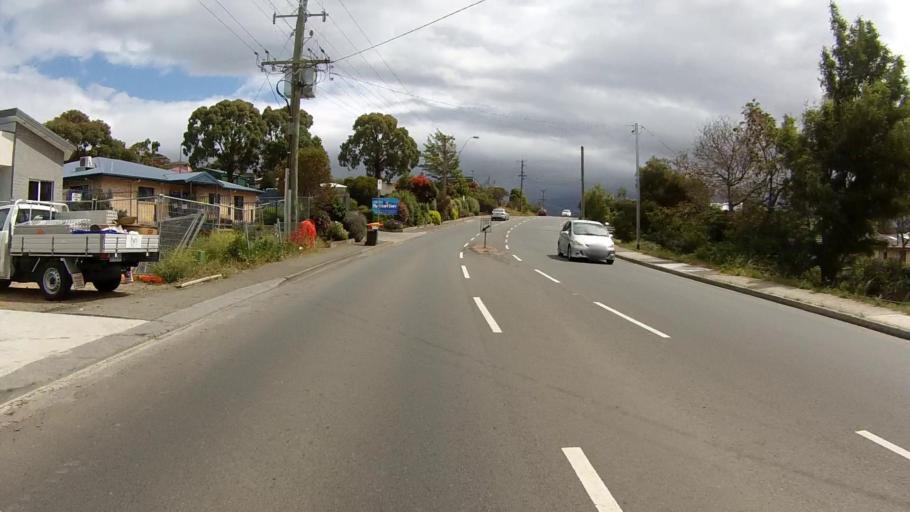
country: AU
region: Tasmania
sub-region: Clarence
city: Warrane
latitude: -42.8634
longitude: 147.3776
